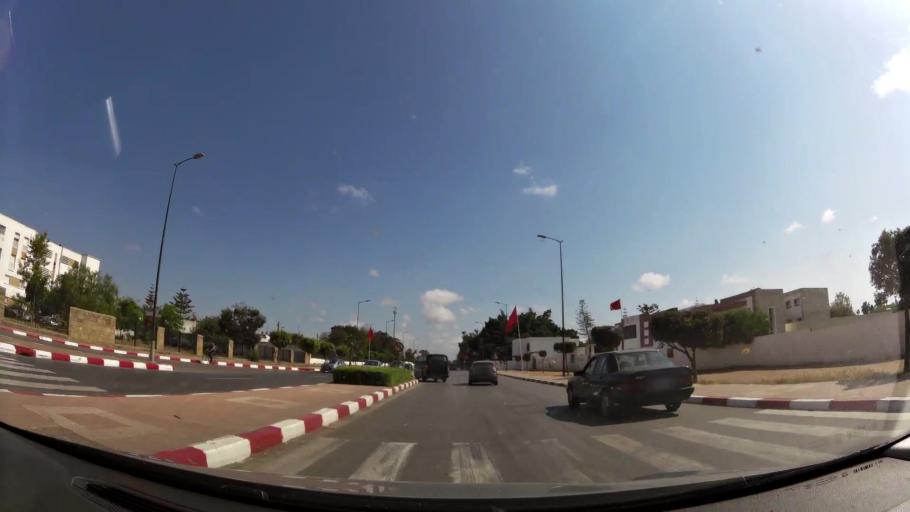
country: MA
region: Rabat-Sale-Zemmour-Zaer
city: Sale
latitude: 34.0415
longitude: -6.7749
